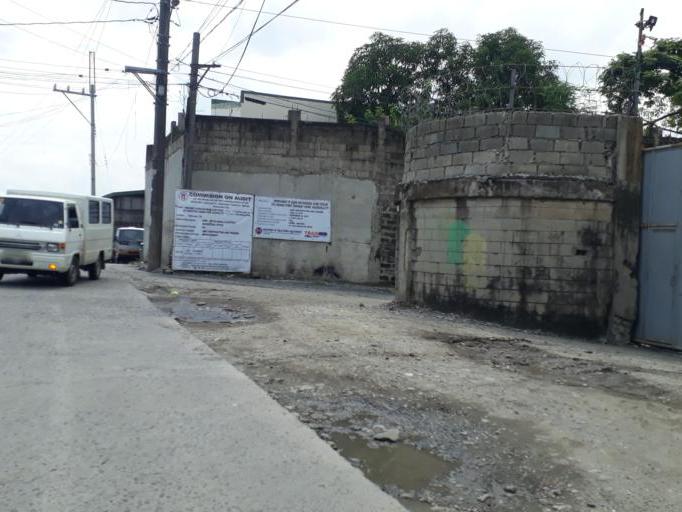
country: PH
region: Calabarzon
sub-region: Province of Rizal
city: Valenzuela
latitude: 14.7052
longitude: 121.0131
